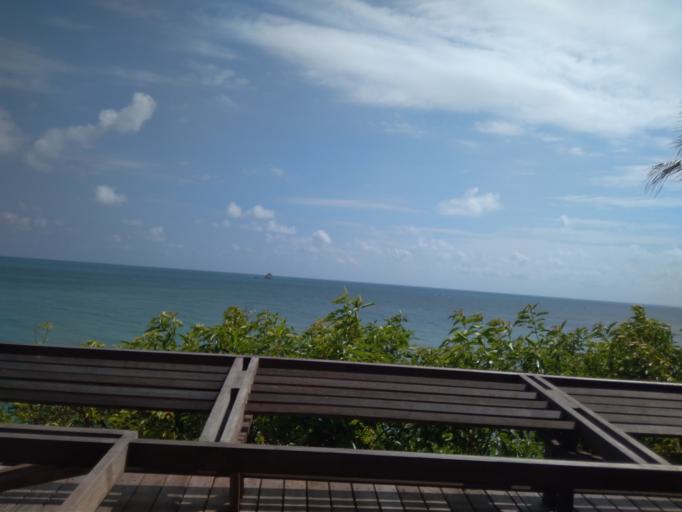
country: TH
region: Surat Thani
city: Ko Samui
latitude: 9.5930
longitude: 100.0689
